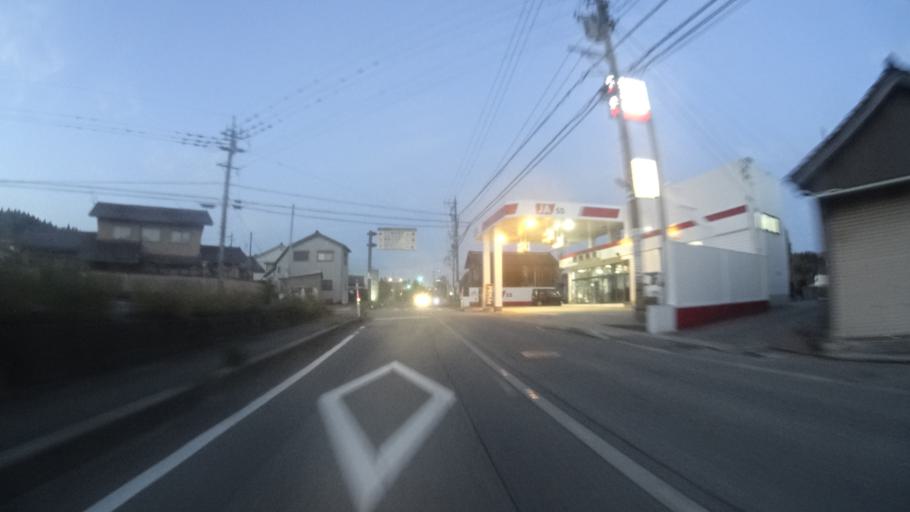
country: JP
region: Ishikawa
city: Nanao
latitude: 37.3876
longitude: 136.8918
